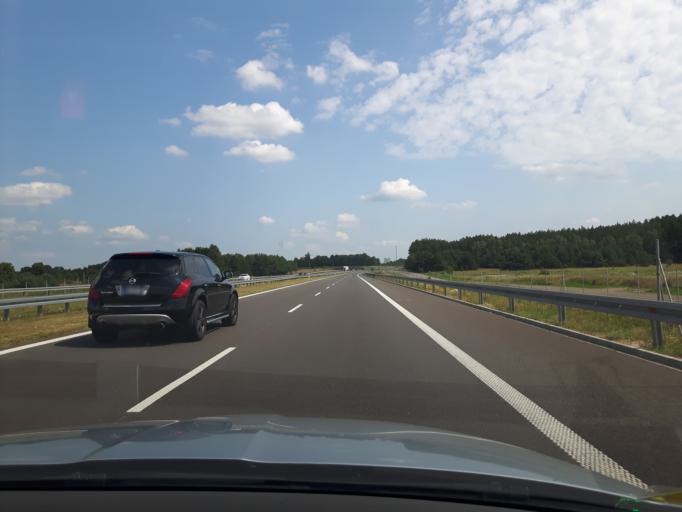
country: PL
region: Warmian-Masurian Voivodeship
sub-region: Powiat olsztynski
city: Olsztynek
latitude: 53.5881
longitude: 20.2266
